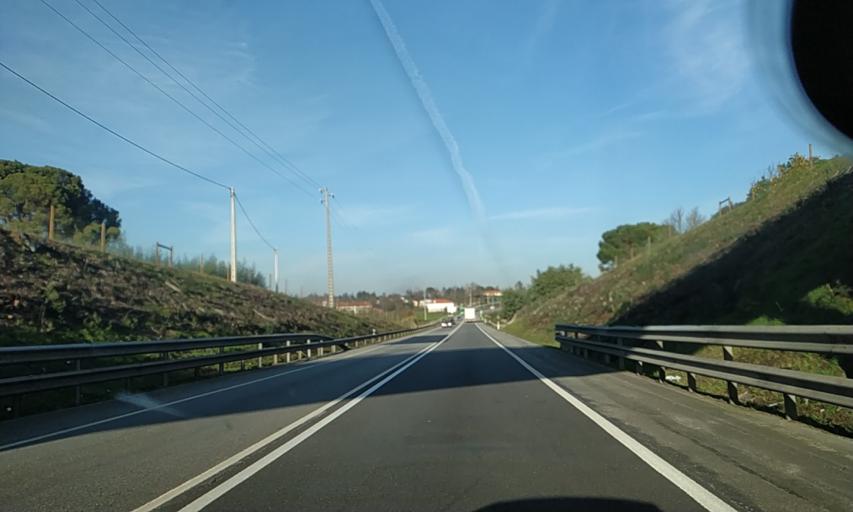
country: PT
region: Viseu
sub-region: Concelho de Tondela
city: Tondela
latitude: 40.5210
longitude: -8.0927
